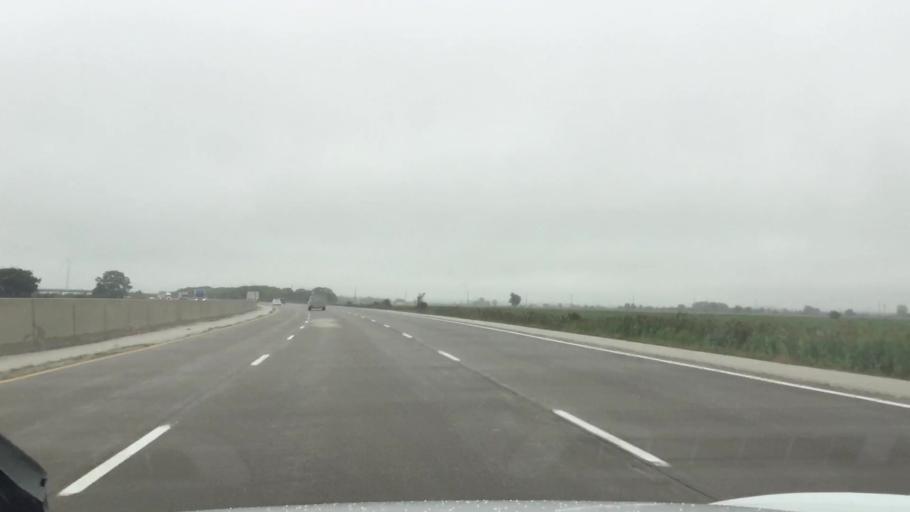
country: US
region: Michigan
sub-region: Wayne County
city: Grosse Pointe Farms
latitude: 42.2320
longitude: -82.6079
